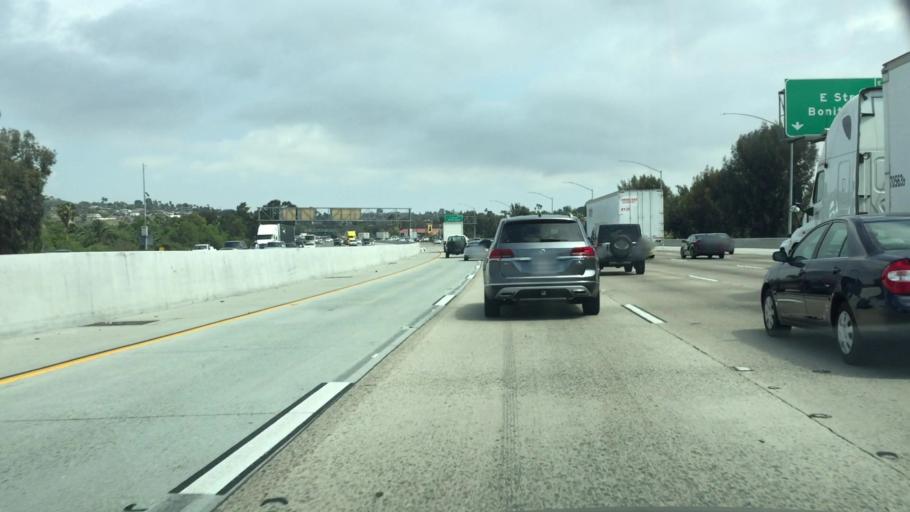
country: US
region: California
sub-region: San Diego County
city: Chula Vista
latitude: 32.6520
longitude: -117.0688
